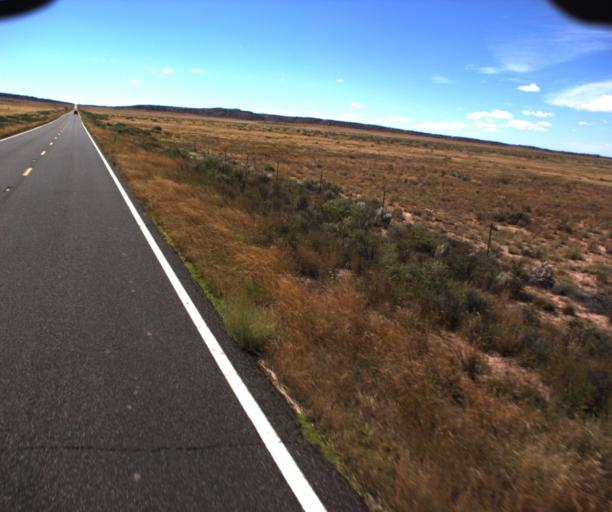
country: US
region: Arizona
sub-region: Apache County
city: Saint Johns
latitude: 34.6859
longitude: -109.2794
